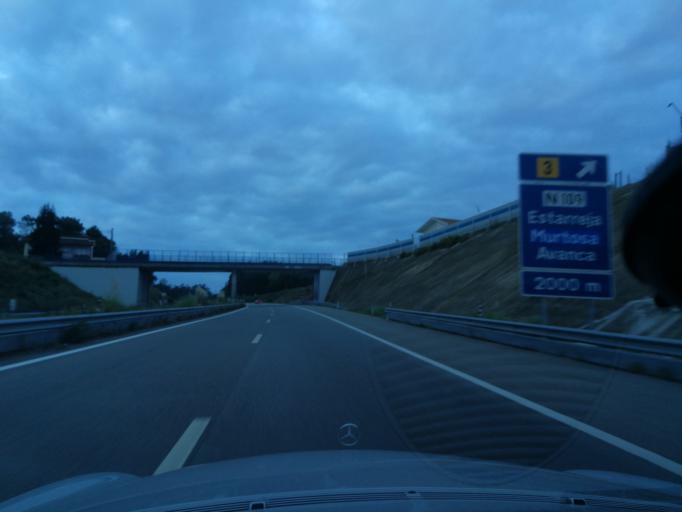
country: PT
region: Aveiro
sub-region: Estarreja
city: Beduido
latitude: 40.7677
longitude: -8.5544
